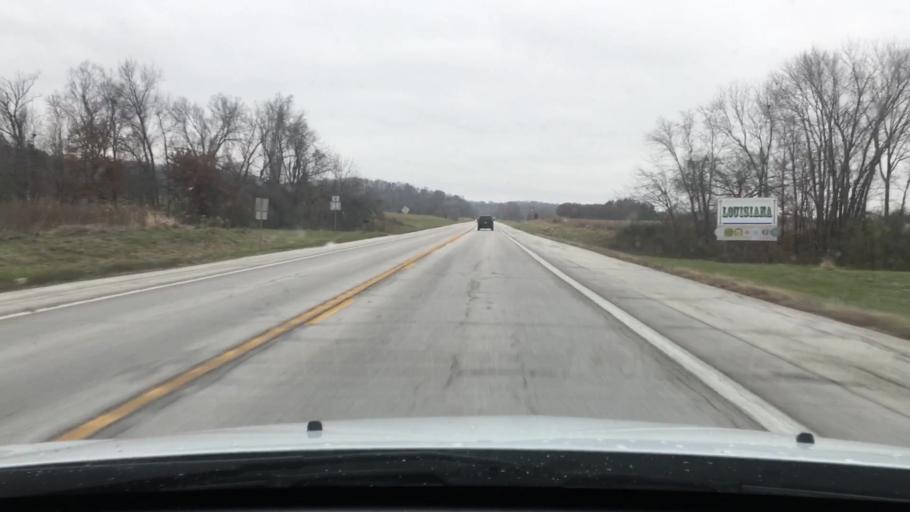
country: US
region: Missouri
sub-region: Pike County
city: Louisiana
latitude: 39.4226
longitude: -91.0862
